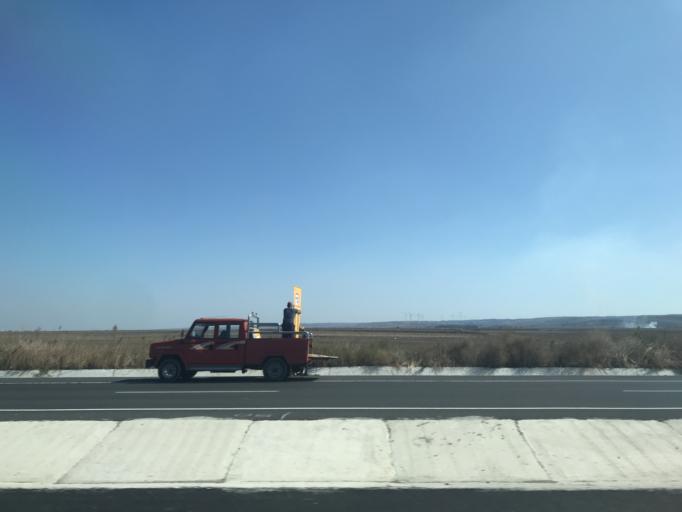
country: TR
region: Tekirdag
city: Muratli
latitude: 41.1691
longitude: 27.5349
